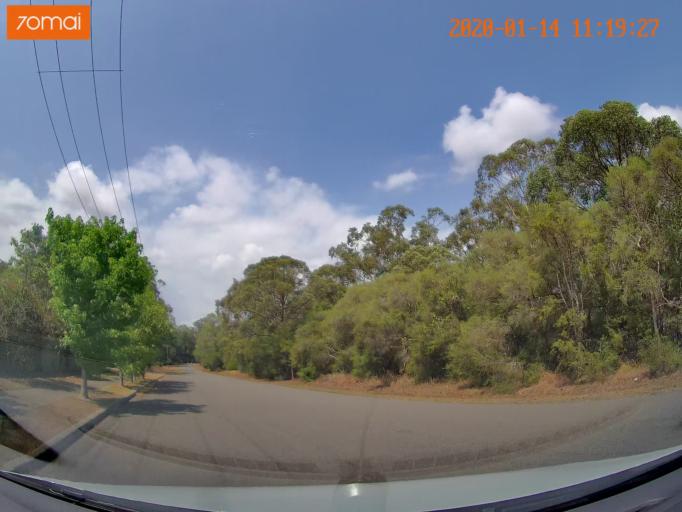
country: AU
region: New South Wales
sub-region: Lake Macquarie Shire
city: Cooranbong
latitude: -33.0980
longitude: 151.4602
